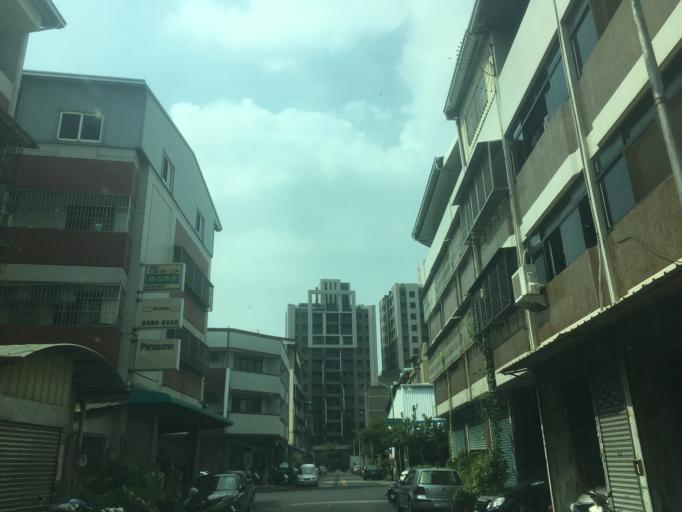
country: TW
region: Taiwan
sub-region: Taichung City
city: Taichung
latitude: 24.1689
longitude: 120.6778
